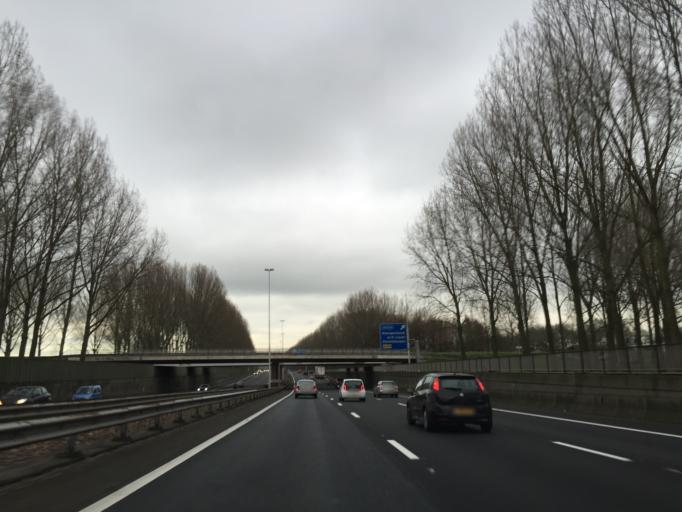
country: NL
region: South Holland
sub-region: Gemeente Capelle aan den IJssel
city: Capelle aan den IJssel
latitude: 51.9713
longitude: 4.6005
